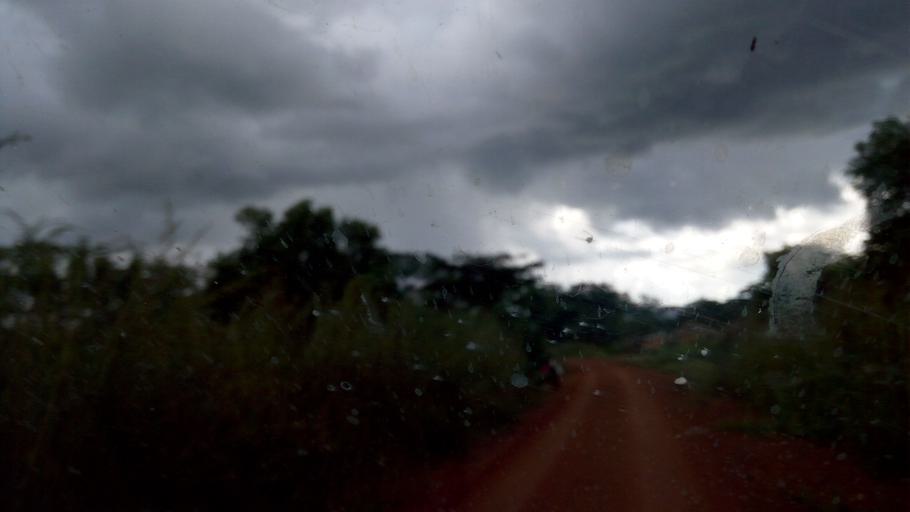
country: ZM
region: Northern
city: Kaputa
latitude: -8.0721
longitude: 29.1691
